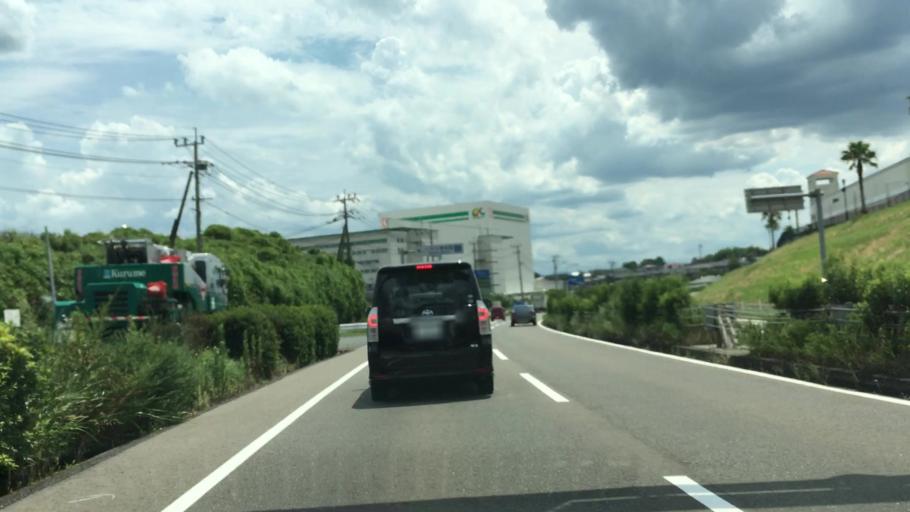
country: JP
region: Saga Prefecture
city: Tosu
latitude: 33.4063
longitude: 130.5131
